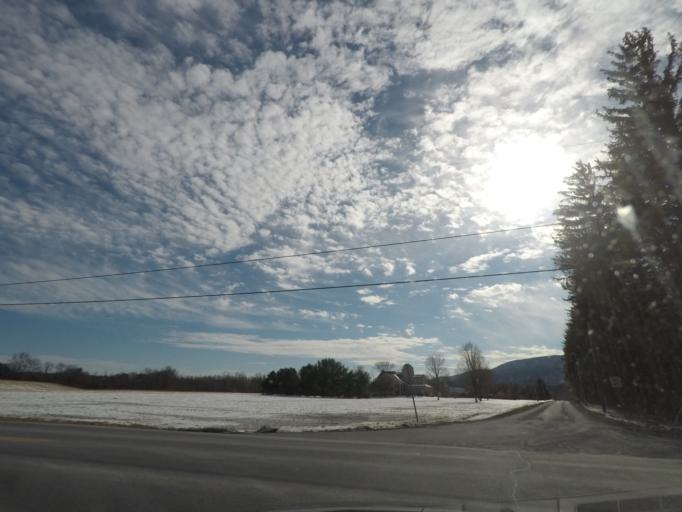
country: US
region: New York
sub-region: Albany County
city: Voorheesville
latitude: 42.6543
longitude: -73.9658
